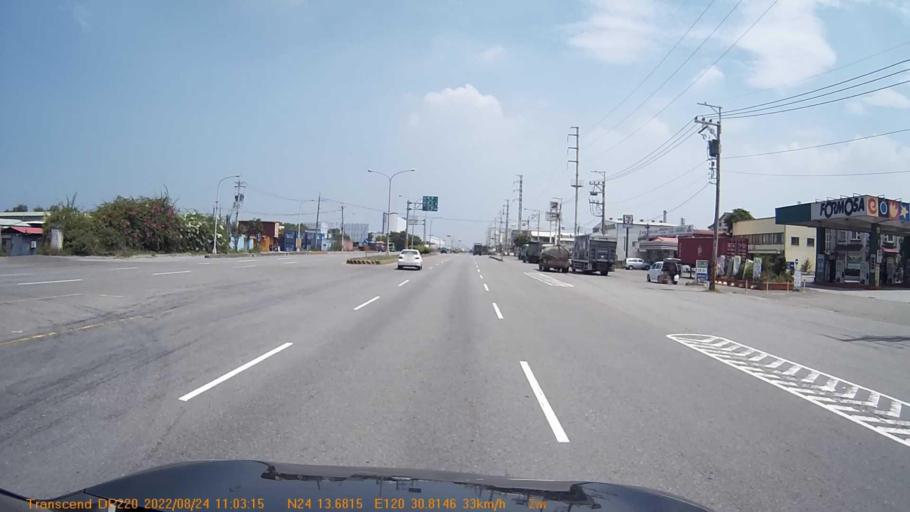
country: TW
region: Taiwan
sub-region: Changhua
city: Chang-hua
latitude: 24.2284
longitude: 120.5137
